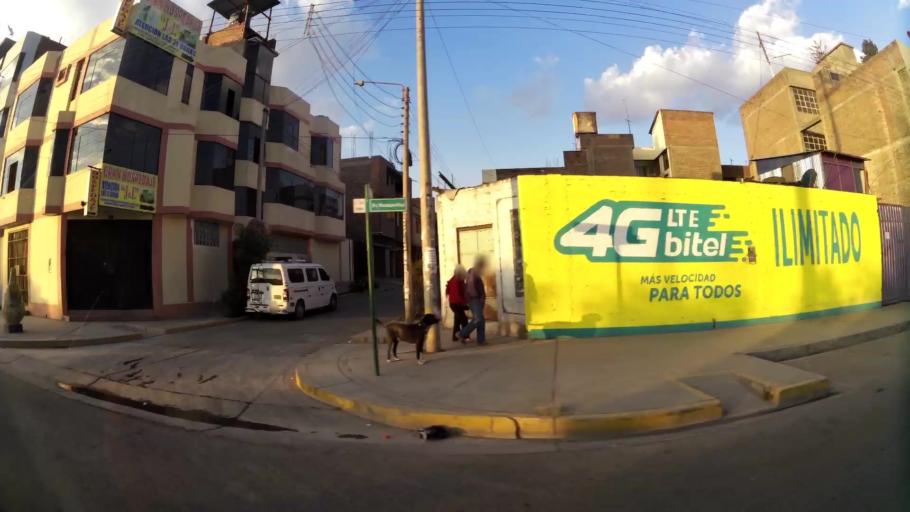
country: PE
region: Junin
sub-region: Provincia de Huancayo
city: El Tambo
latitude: -12.0517
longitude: -75.2271
